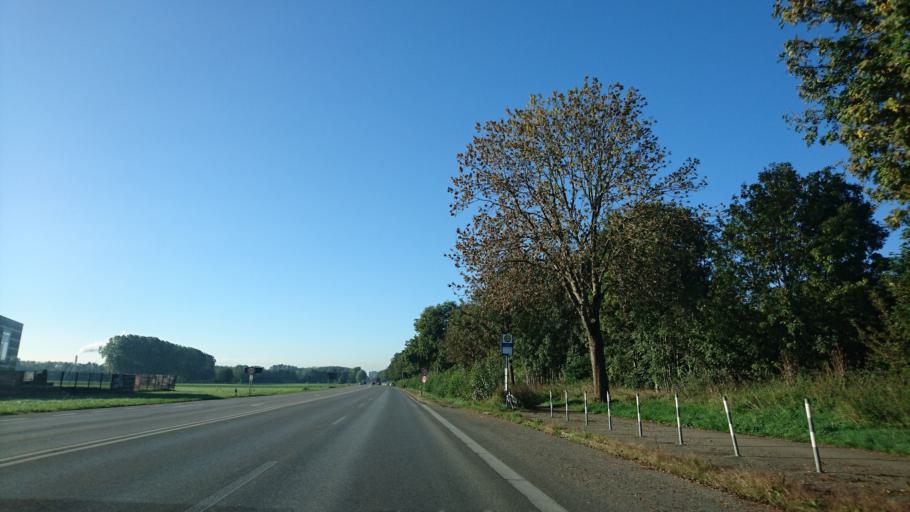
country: DE
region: Bavaria
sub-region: Swabia
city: Gersthofen
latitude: 48.4205
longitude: 10.9199
